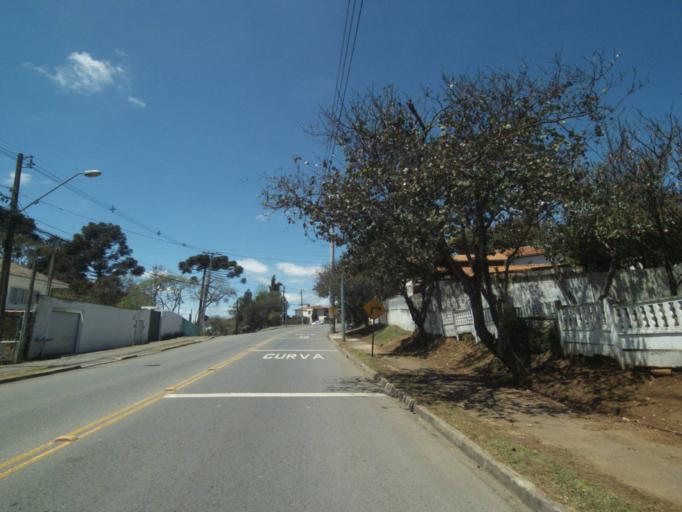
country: BR
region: Parana
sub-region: Curitiba
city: Curitiba
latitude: -25.3883
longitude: -49.2732
